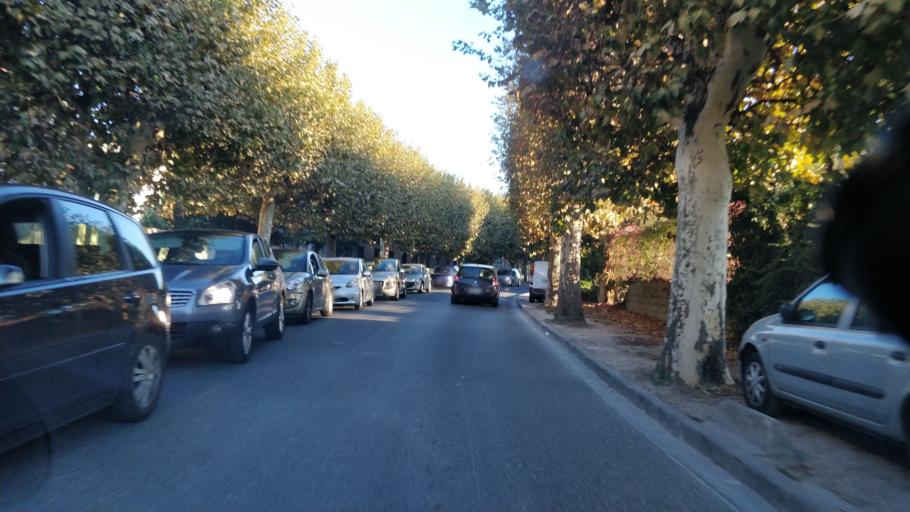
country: FR
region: Ile-de-France
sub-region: Departement de Seine-Saint-Denis
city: Gournay-sur-Marne
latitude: 48.8683
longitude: 2.5744
